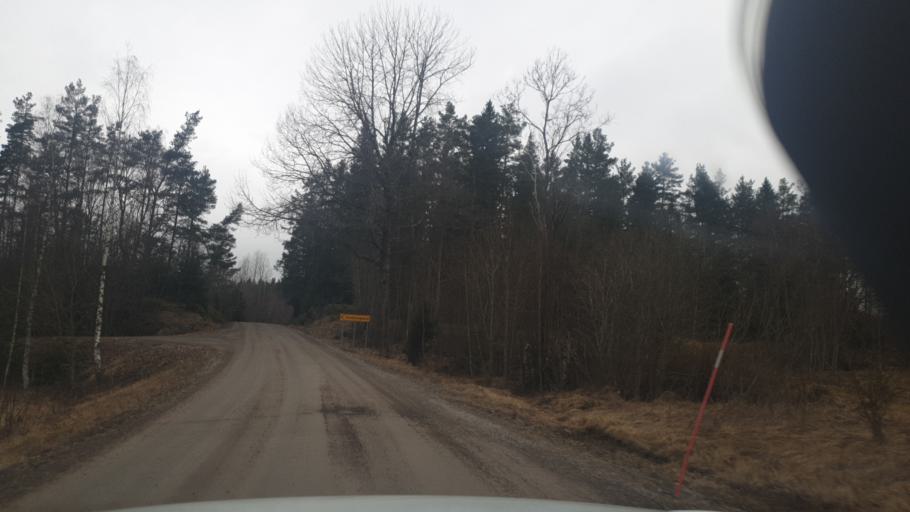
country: NO
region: Hedmark
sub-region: Eidskog
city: Skotterud
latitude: 59.7303
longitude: 12.1013
